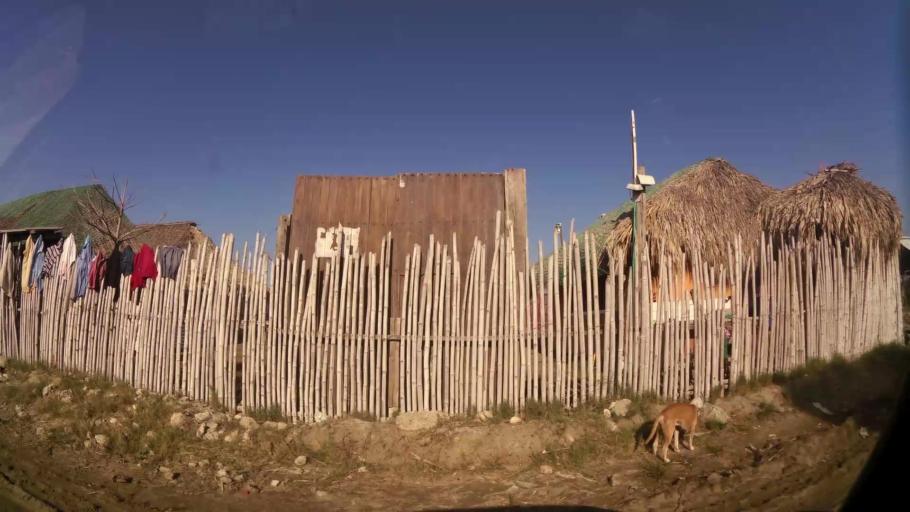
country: CO
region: Bolivar
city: Cartagena
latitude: 10.4828
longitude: -75.4930
